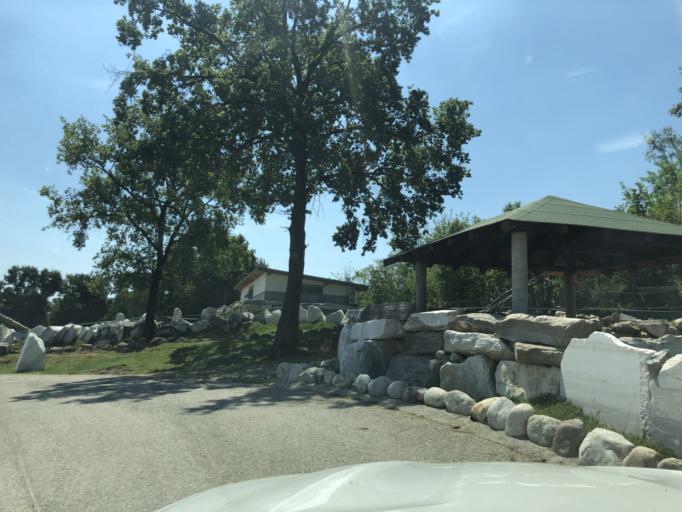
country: IT
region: Piedmont
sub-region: Provincia di Novara
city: Mezzomerico
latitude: 45.6401
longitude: 8.6091
